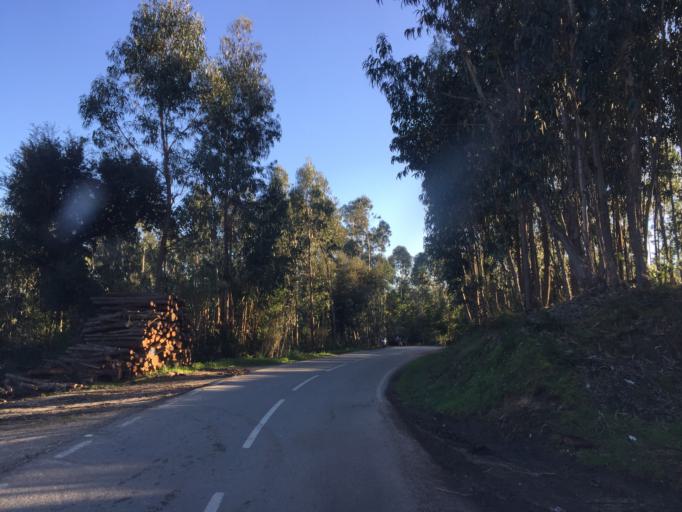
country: PT
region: Coimbra
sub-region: Figueira da Foz
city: Alhadas
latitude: 40.1592
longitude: -8.8008
